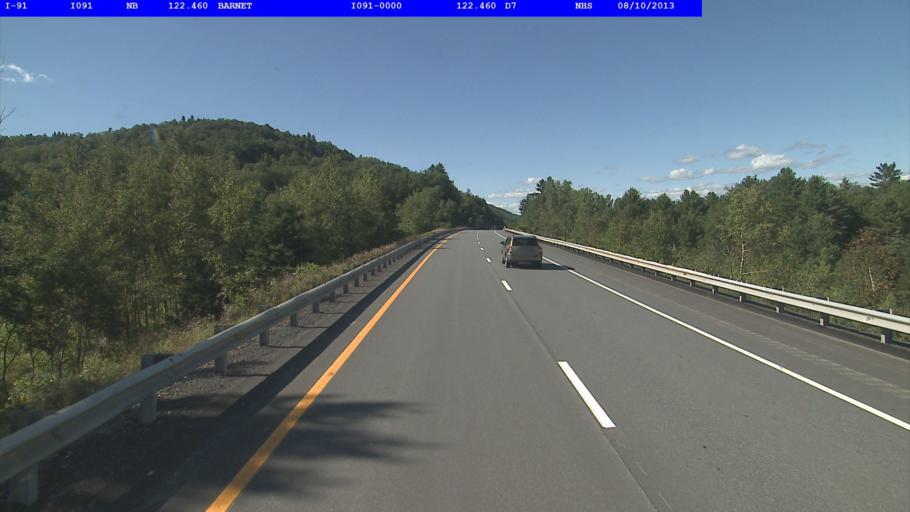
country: US
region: Vermont
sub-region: Caledonia County
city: Saint Johnsbury
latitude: 44.3170
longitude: -72.0368
